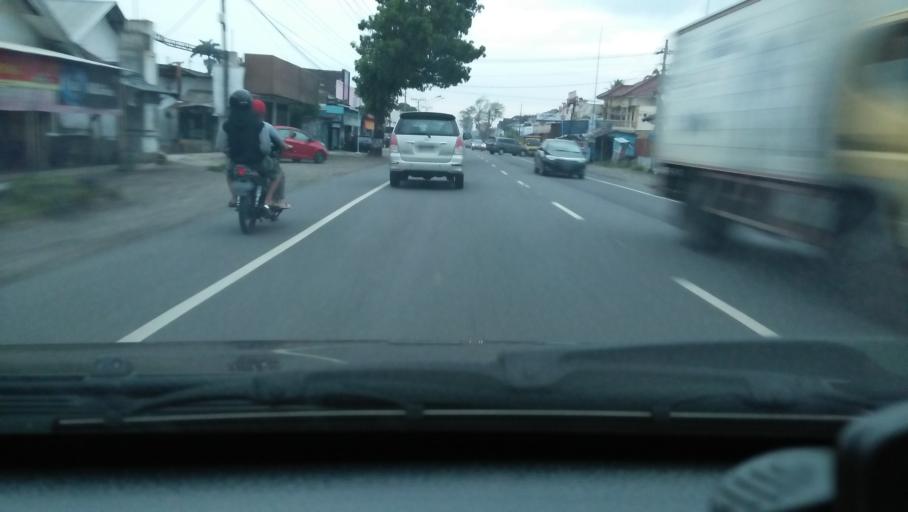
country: ID
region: Central Java
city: Magelang
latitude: -7.3961
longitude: 110.2450
